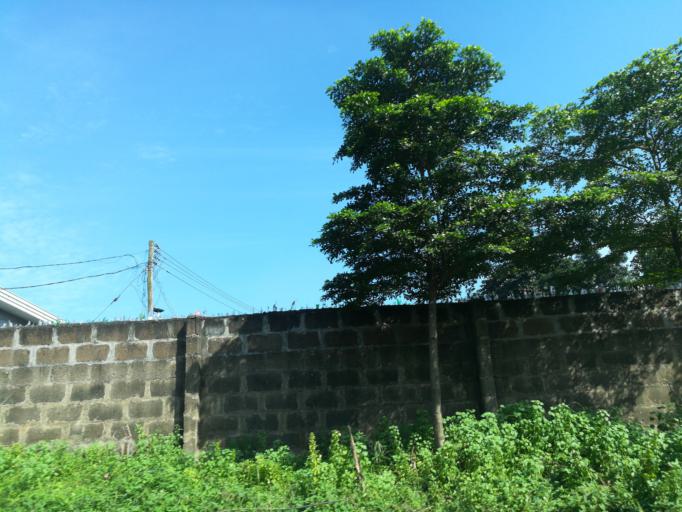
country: NG
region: Lagos
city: Ikeja
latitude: 6.6034
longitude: 3.3407
